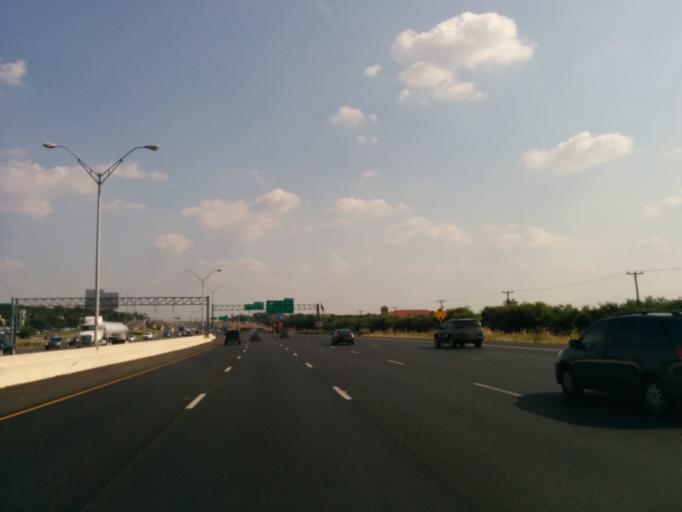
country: US
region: Texas
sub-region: Bexar County
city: Shavano Park
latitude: 29.5851
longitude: -98.5977
